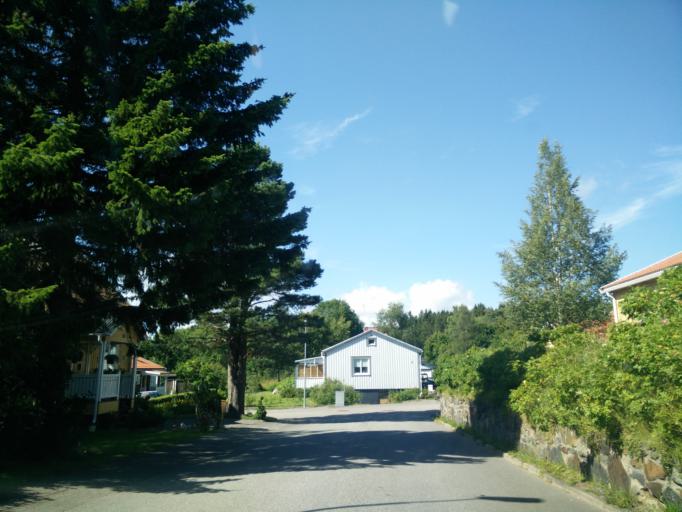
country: SE
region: Vaesternorrland
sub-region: Haernoesands Kommun
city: Haernoesand
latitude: 62.6335
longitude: 17.9096
